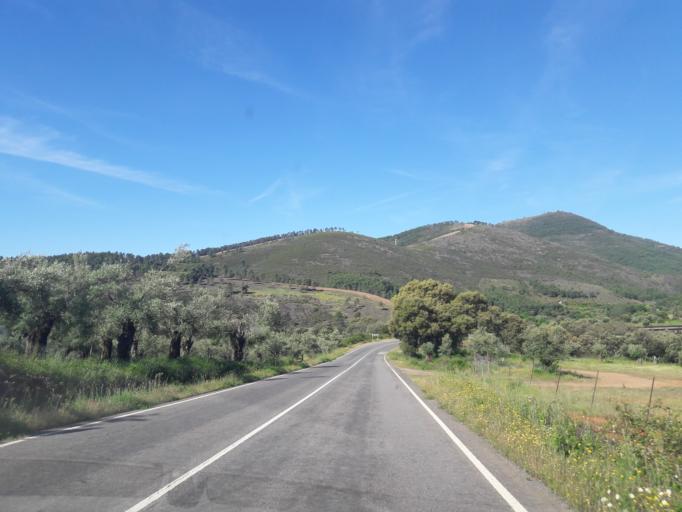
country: ES
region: Castille and Leon
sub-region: Provincia de Salamanca
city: Herguijuela de la Sierra
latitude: 40.4042
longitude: -6.0715
